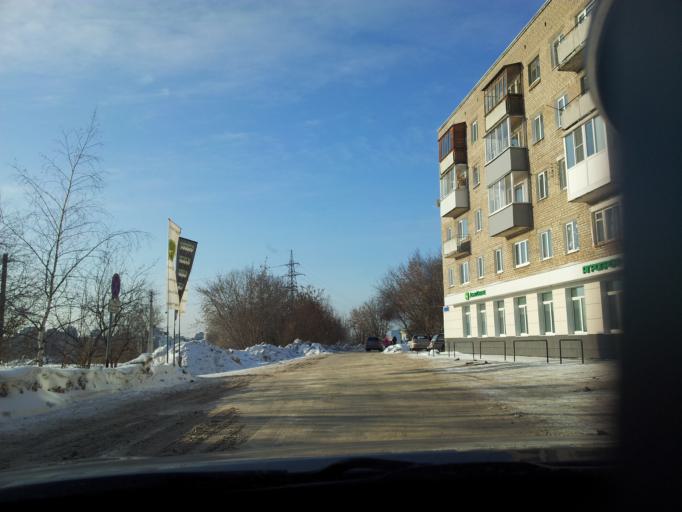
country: RU
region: Perm
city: Perm
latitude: 58.0209
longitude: 56.2707
